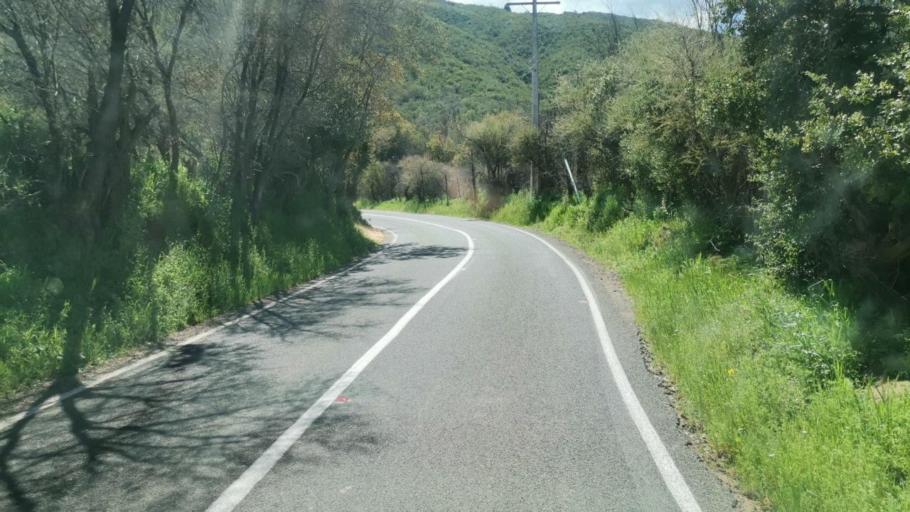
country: CL
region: Valparaiso
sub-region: Provincia de Marga Marga
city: Limache
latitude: -33.1808
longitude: -71.1853
